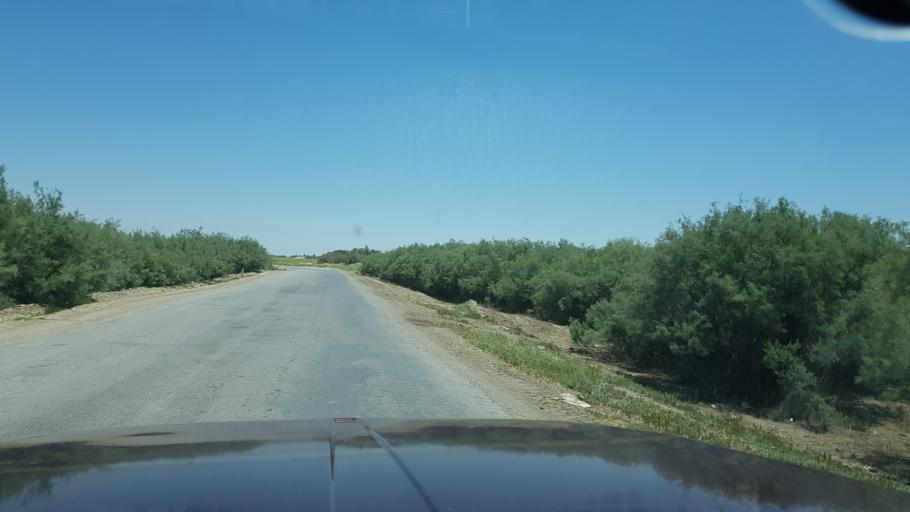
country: TM
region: Ahal
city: Annau
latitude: 37.8835
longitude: 58.7426
